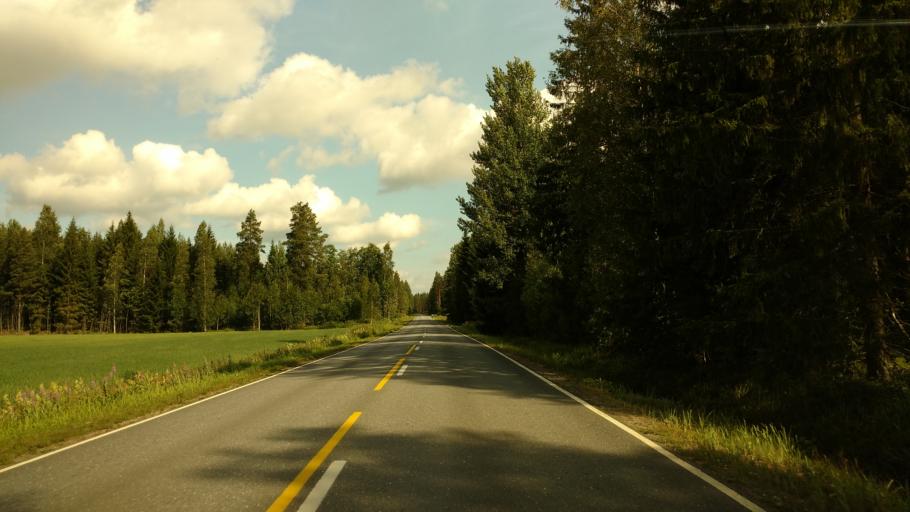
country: FI
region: Varsinais-Suomi
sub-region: Loimaa
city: Koski Tl
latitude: 60.6065
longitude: 23.1227
